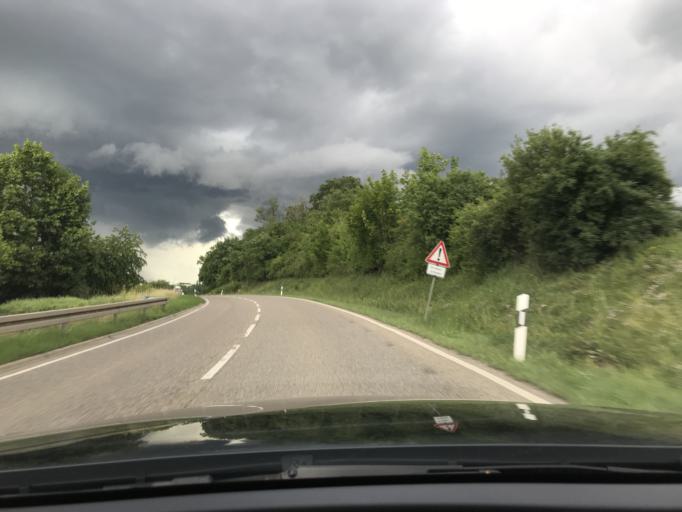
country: DE
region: Baden-Wuerttemberg
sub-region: Regierungsbezirk Stuttgart
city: Stuttgart Muehlhausen
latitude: 48.8611
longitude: 9.2649
